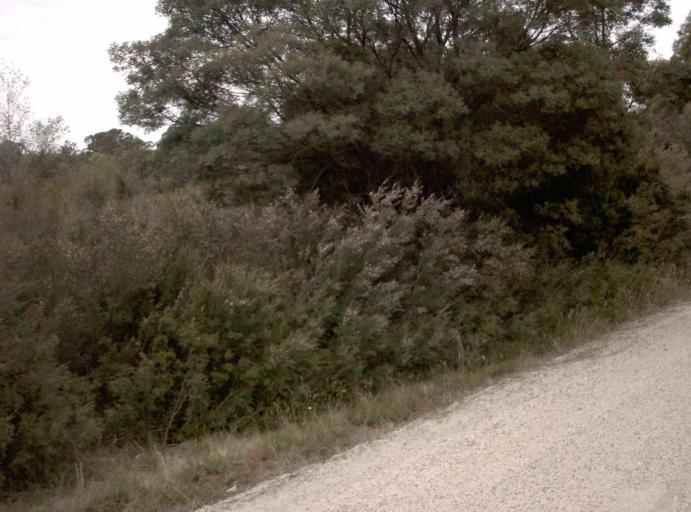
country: AU
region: Victoria
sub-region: Wellington
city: Sale
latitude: -38.1860
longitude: 147.2727
